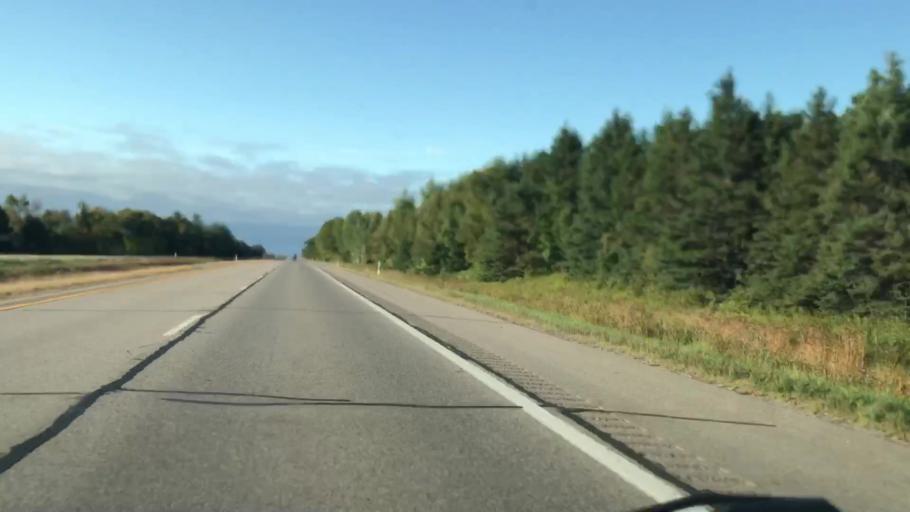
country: US
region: Michigan
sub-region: Chippewa County
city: Sault Ste. Marie
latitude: 46.4382
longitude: -84.3882
